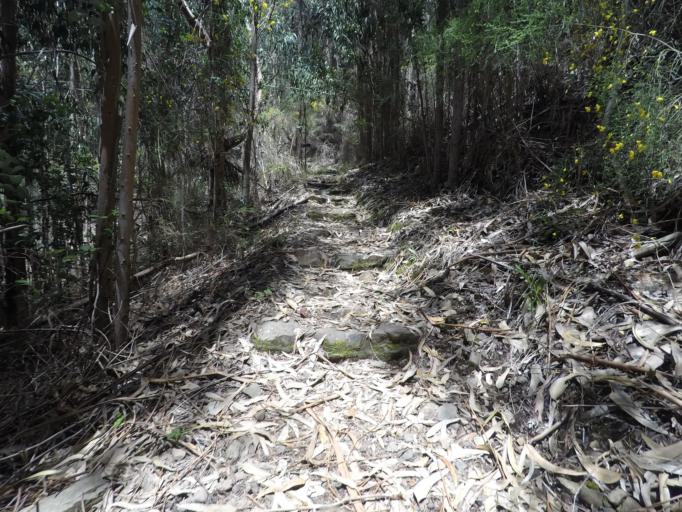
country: PT
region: Madeira
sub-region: Camara de Lobos
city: Curral das Freiras
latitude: 32.7515
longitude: -16.9699
